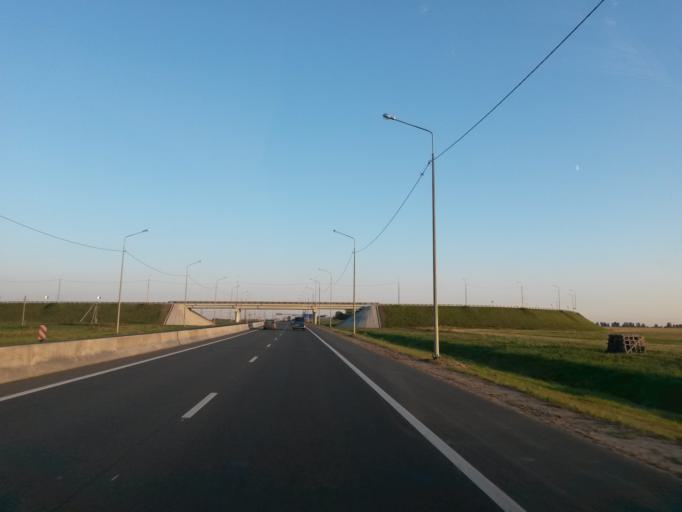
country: RU
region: Jaroslavl
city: Yaroslavl
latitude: 57.7256
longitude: 39.8998
